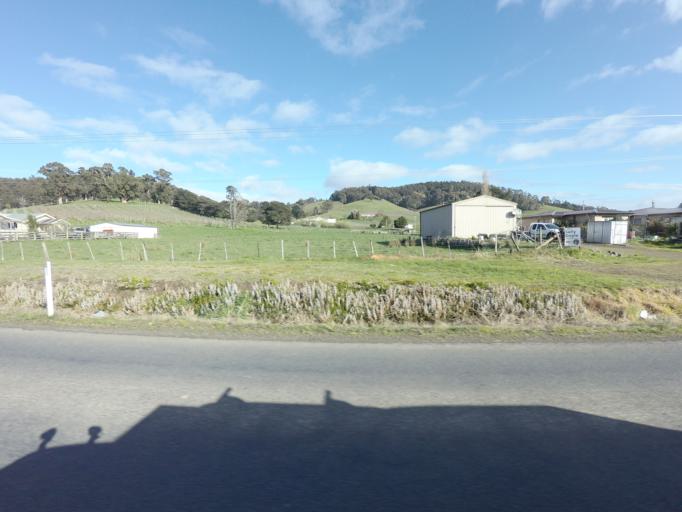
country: AU
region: Tasmania
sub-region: Huon Valley
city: Geeveston
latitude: -43.1910
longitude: 146.9598
